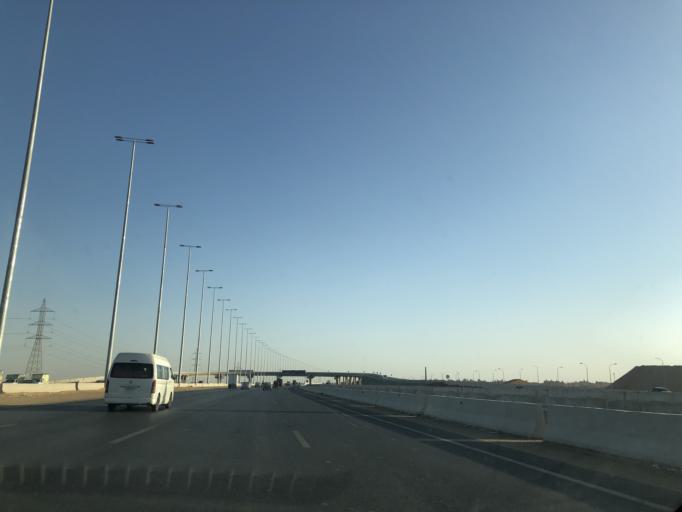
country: EG
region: Al Jizah
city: Madinat Sittah Uktubar
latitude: 29.9307
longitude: 31.0968
